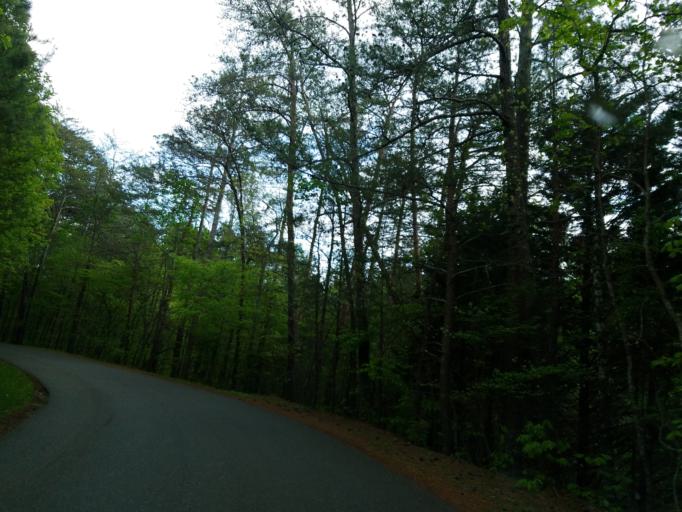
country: US
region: Georgia
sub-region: Pickens County
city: Jasper
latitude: 34.4409
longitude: -84.4847
